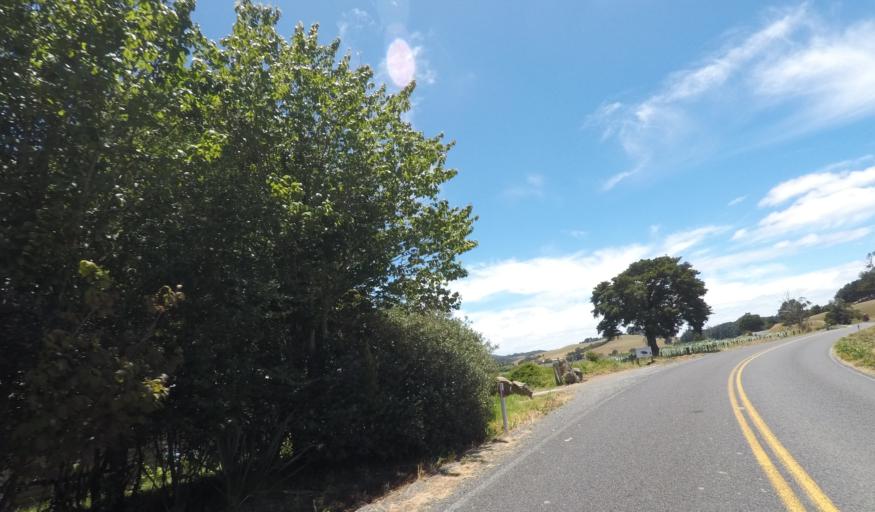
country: NZ
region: Northland
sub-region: Whangarei
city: Whangarei
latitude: -35.5515
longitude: 174.2966
